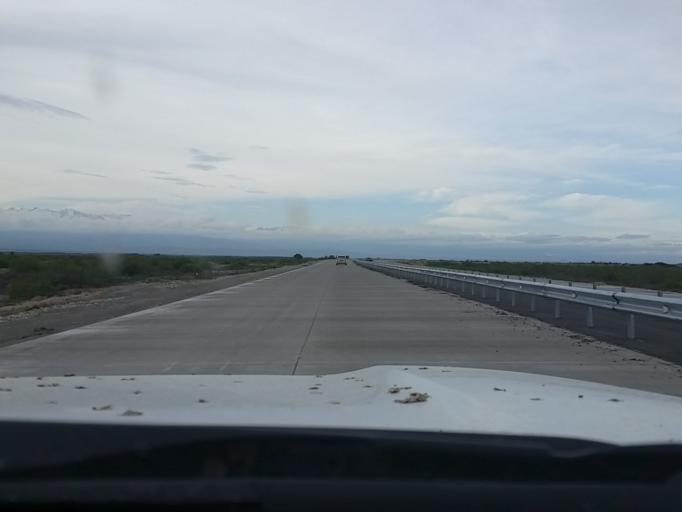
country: KZ
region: Almaty Oblysy
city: Zharkent
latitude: 44.0940
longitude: 80.0580
